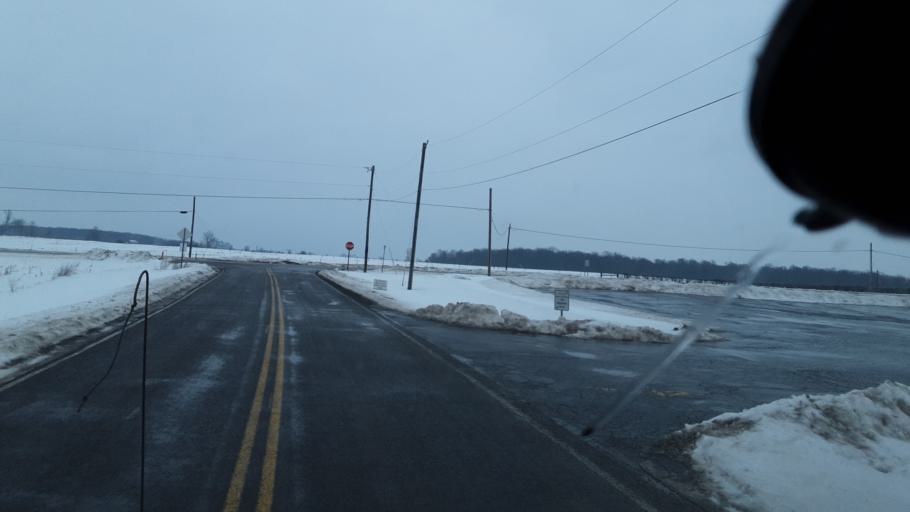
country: US
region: Ohio
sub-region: Union County
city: Marysville
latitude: 40.1896
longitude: -83.3526
